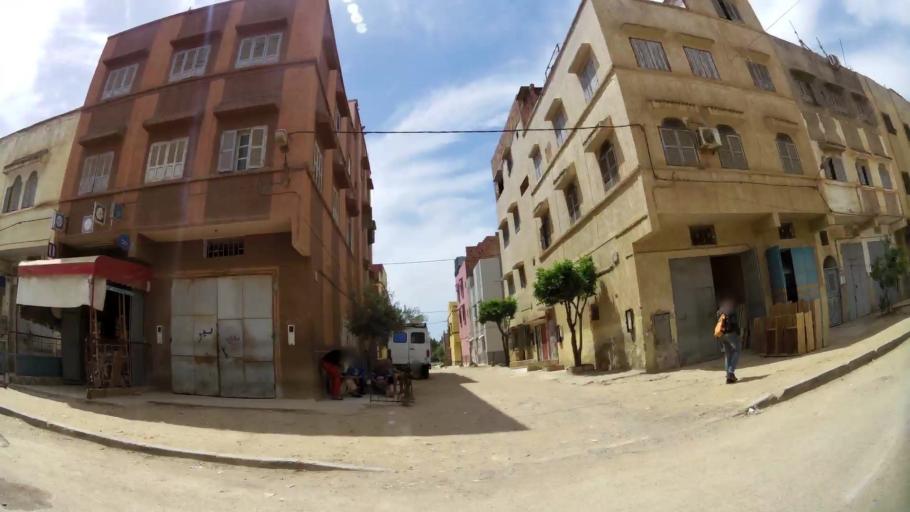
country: MA
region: Rabat-Sale-Zemmour-Zaer
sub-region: Khemisset
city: Khemisset
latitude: 33.8152
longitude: -6.0682
